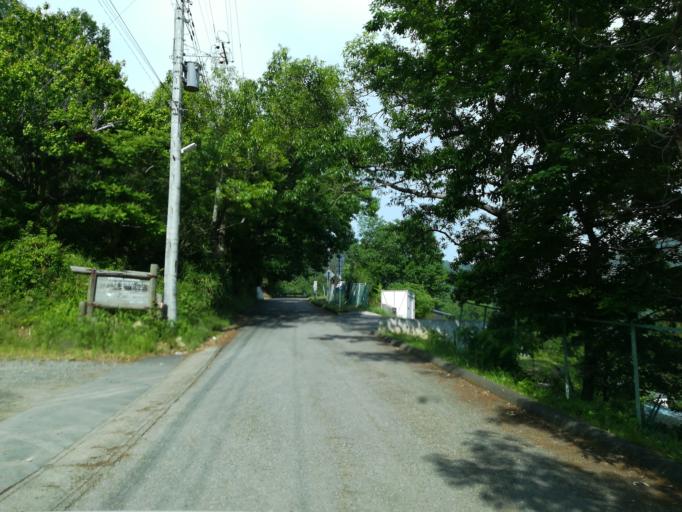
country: JP
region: Ibaraki
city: Tsukuba
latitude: 36.1822
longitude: 140.1109
